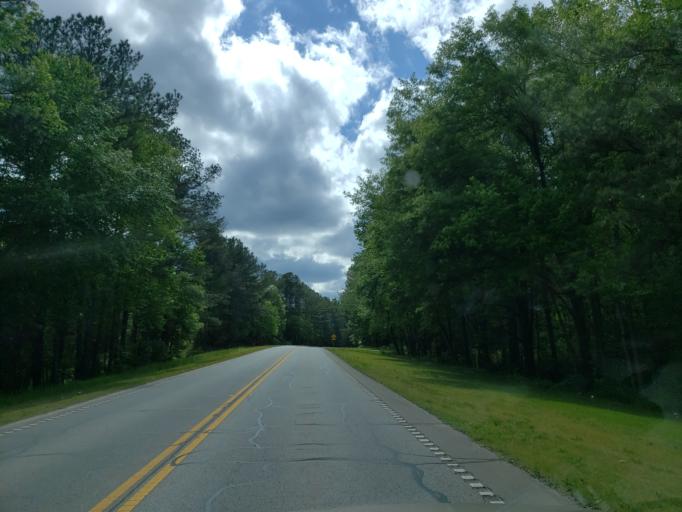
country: US
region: Georgia
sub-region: Haralson County
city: Tallapoosa
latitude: 33.7404
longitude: -85.3304
